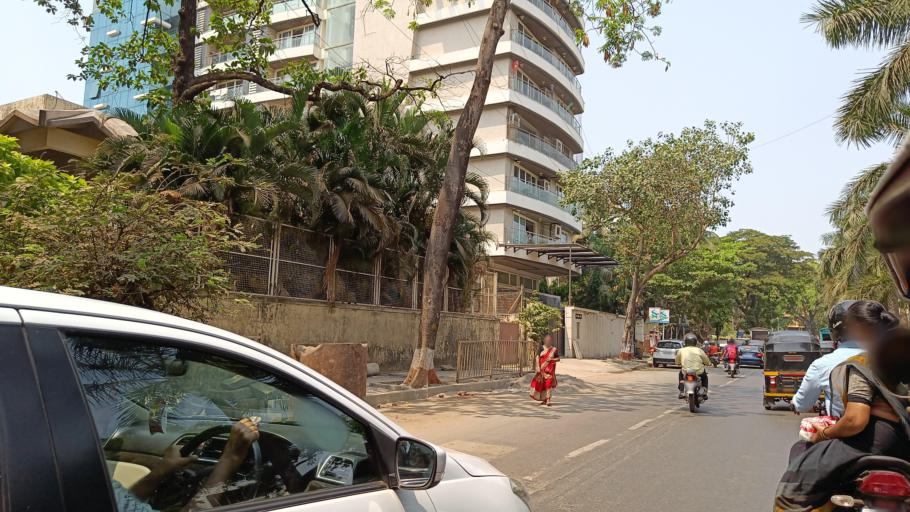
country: IN
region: Maharashtra
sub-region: Mumbai Suburban
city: Mumbai
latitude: 19.1045
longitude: 72.8281
